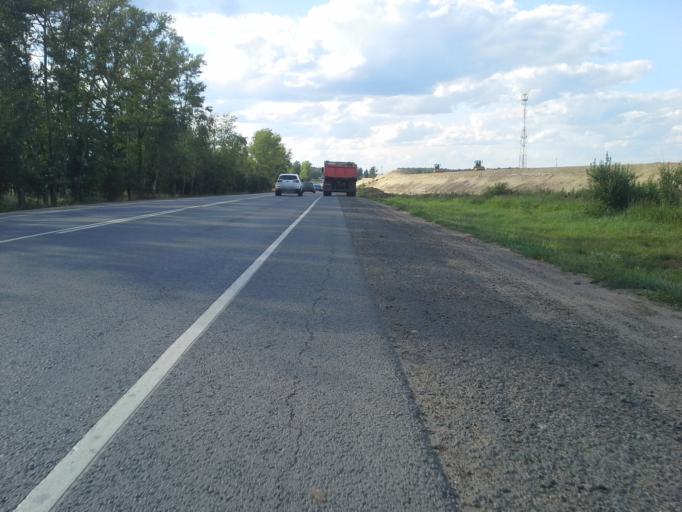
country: RU
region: Moskovskaya
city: Klimovsk
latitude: 55.3579
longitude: 37.4368
